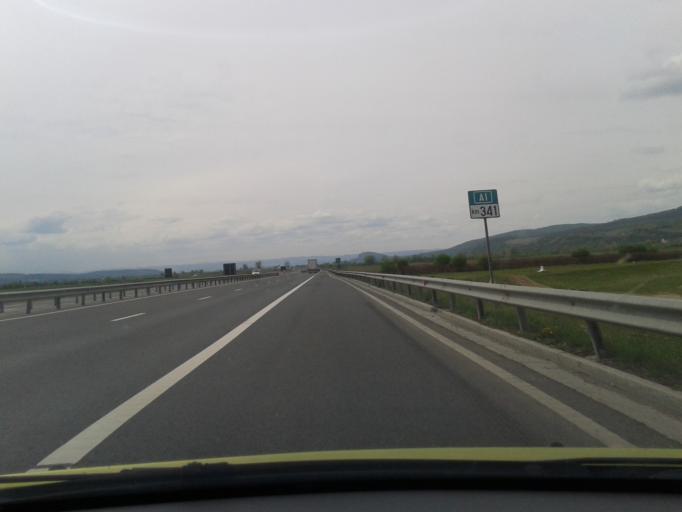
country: RO
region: Hunedoara
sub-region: Comuna Turdas
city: Pricaz
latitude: 45.8768
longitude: 23.1860
